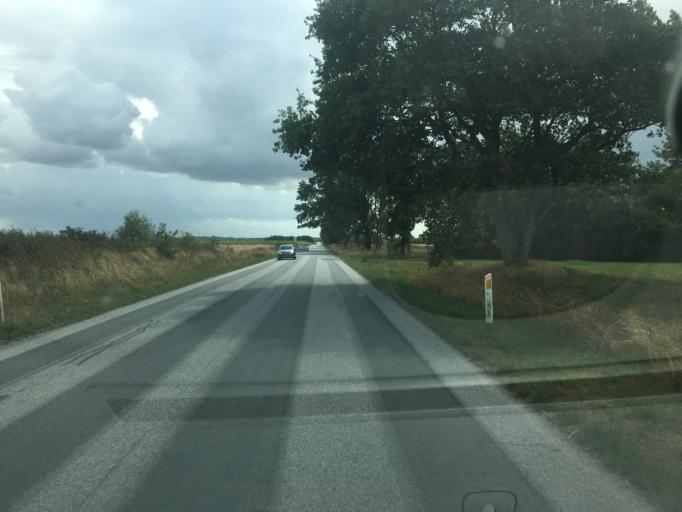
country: DK
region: South Denmark
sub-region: Tonder Kommune
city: Logumkloster
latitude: 55.0501
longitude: 8.9596
